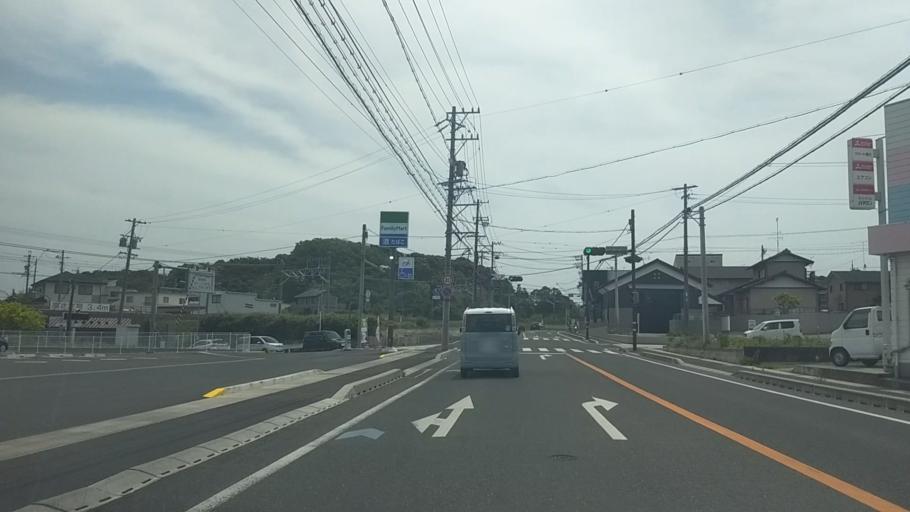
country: JP
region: Shizuoka
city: Kosai-shi
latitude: 34.7014
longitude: 137.5548
